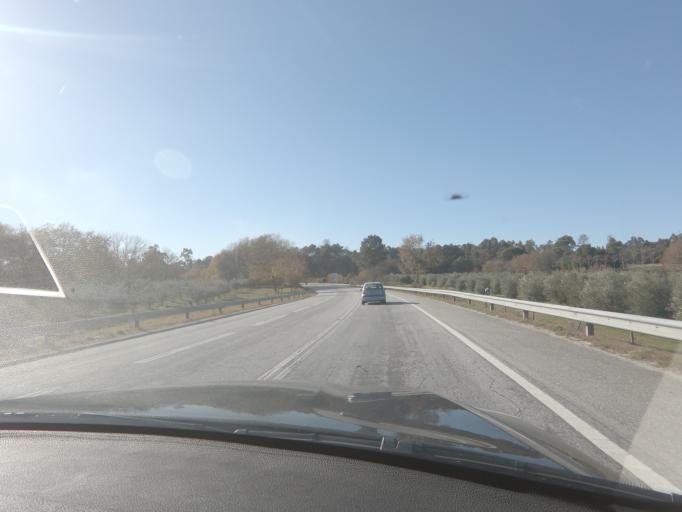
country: PT
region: Viseu
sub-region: Viseu
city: Abraveses
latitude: 40.6751
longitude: -7.9796
